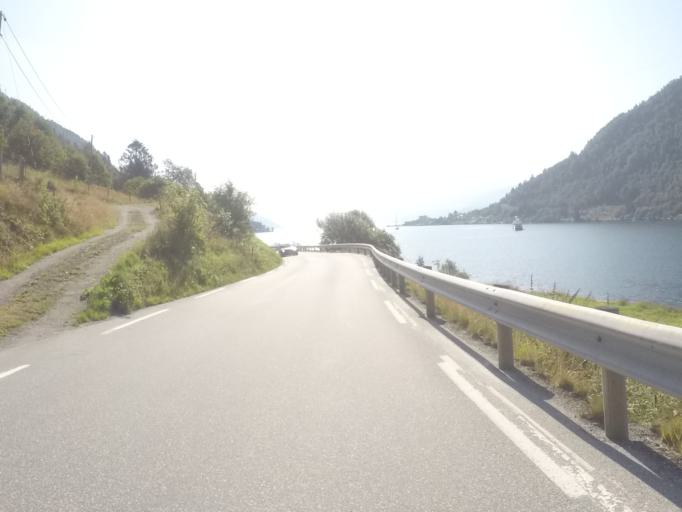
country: NO
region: Sogn og Fjordane
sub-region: Balestrand
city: Balestrand
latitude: 61.2198
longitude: 6.5047
